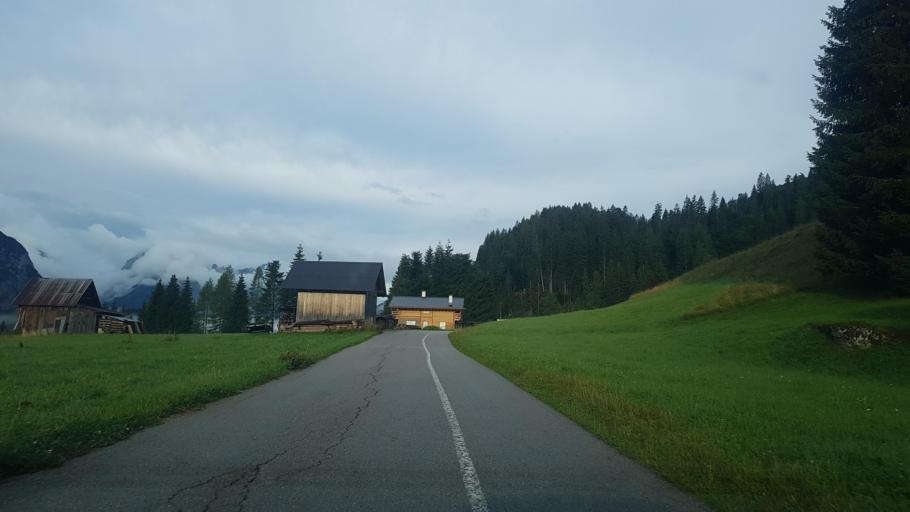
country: IT
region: Veneto
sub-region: Provincia di Belluno
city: Granvilla
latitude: 46.5741
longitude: 12.7269
